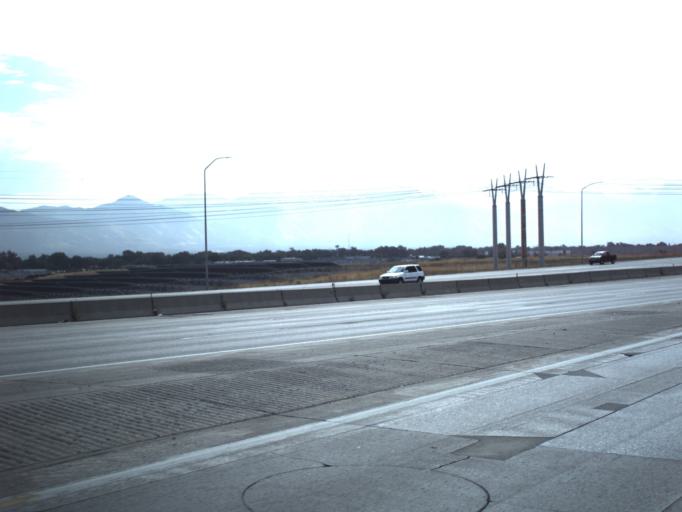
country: US
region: Utah
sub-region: Salt Lake County
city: Salt Lake City
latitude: 40.7571
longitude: -111.9503
